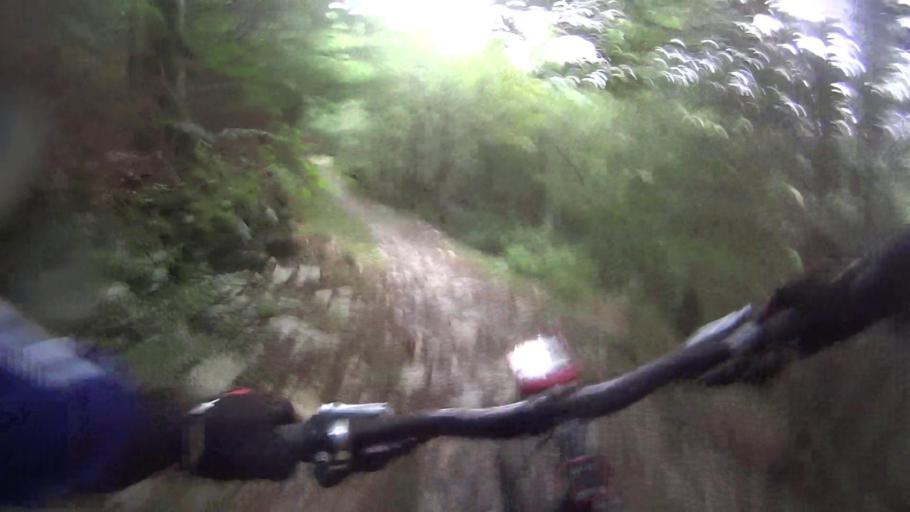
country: GB
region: Wales
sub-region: County of Ceredigion
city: Bow Street
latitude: 52.4185
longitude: -3.9167
